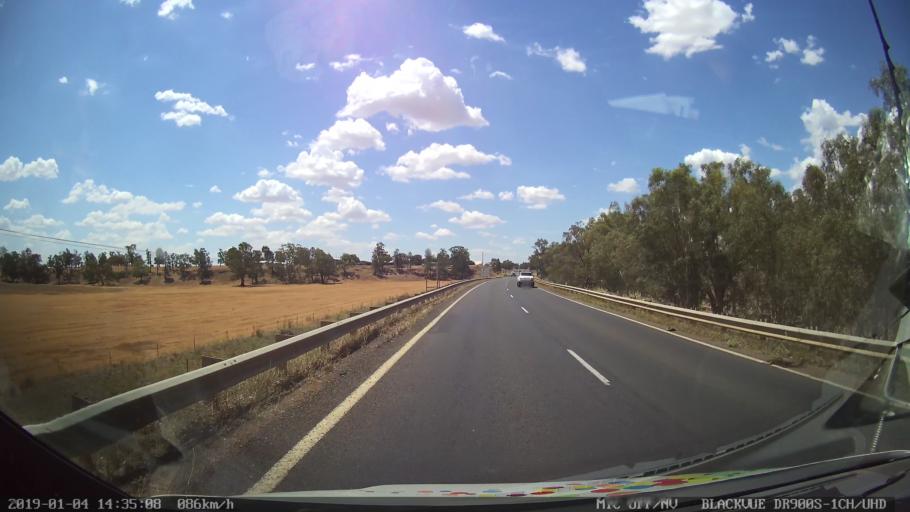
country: AU
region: New South Wales
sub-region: Dubbo Municipality
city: Dubbo
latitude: -32.1894
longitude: 148.6212
